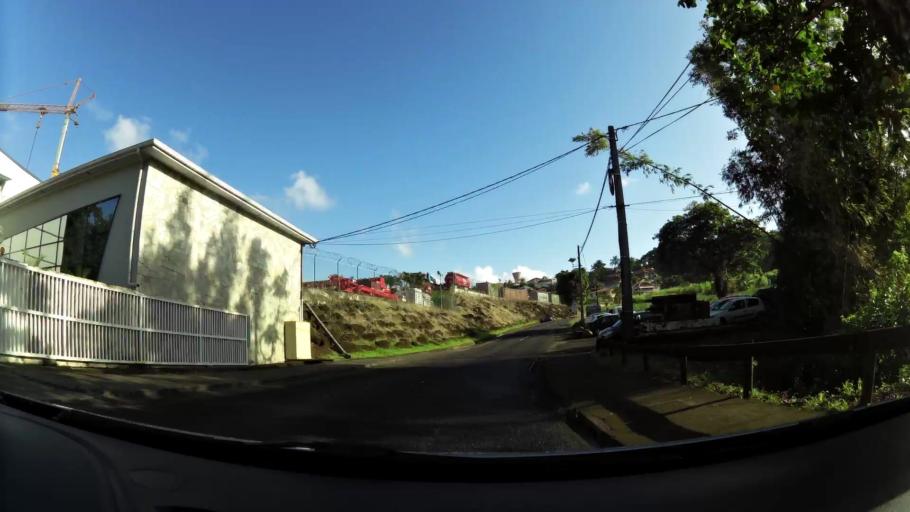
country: MQ
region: Martinique
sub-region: Martinique
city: Le Lamentin
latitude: 14.6331
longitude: -61.0349
